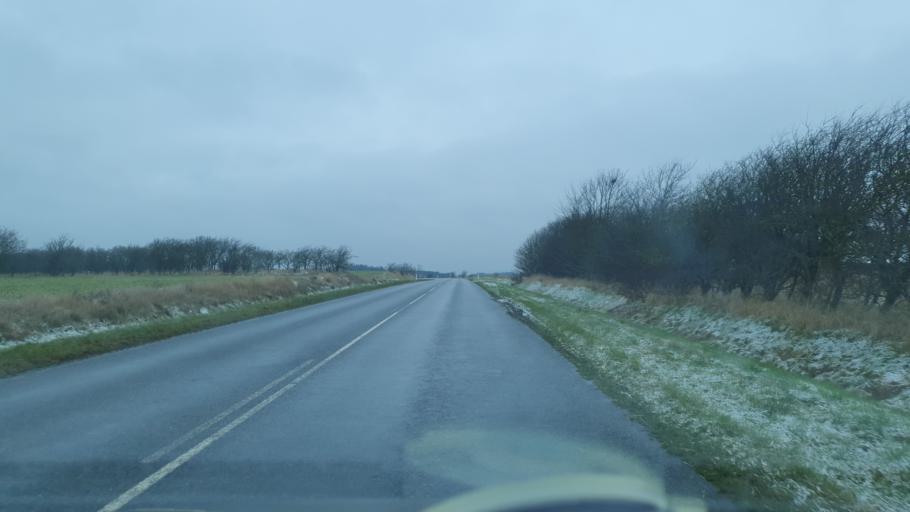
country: DK
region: North Denmark
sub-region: Jammerbugt Kommune
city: Brovst
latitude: 57.1229
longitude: 9.4913
